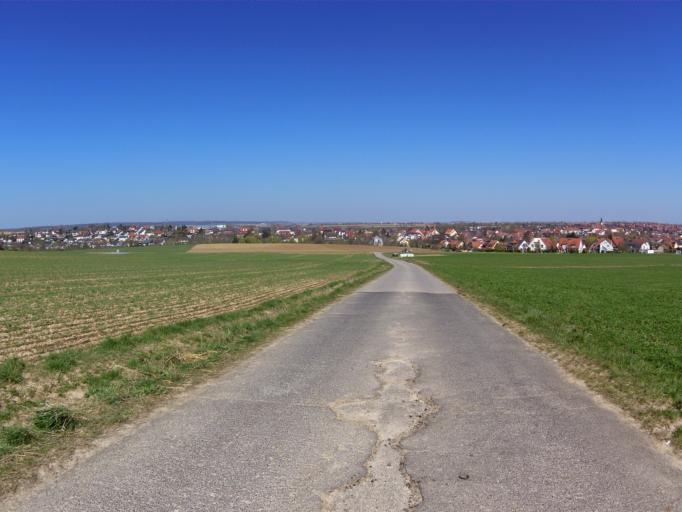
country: DE
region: Bavaria
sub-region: Regierungsbezirk Unterfranken
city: Kurnach
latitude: 49.8384
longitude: 10.0364
